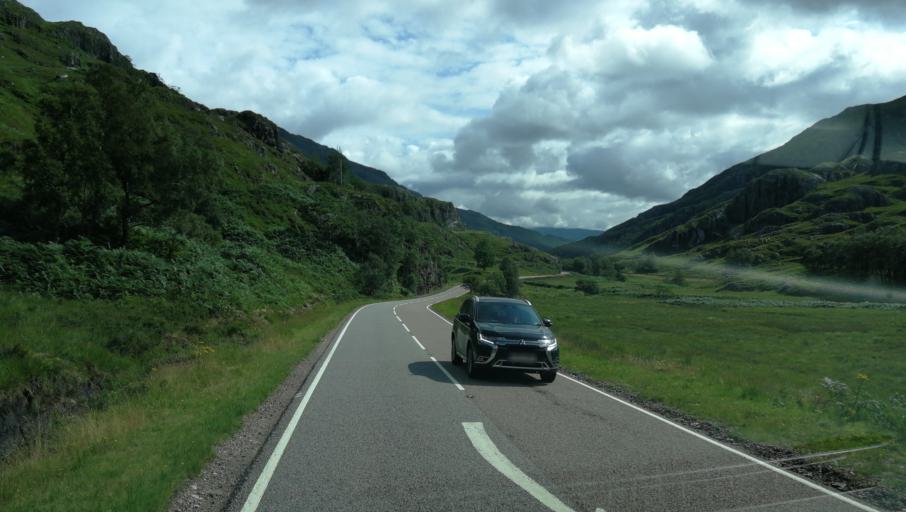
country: GB
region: Scotland
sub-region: Highland
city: Fort William
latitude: 56.8756
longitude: -5.5106
